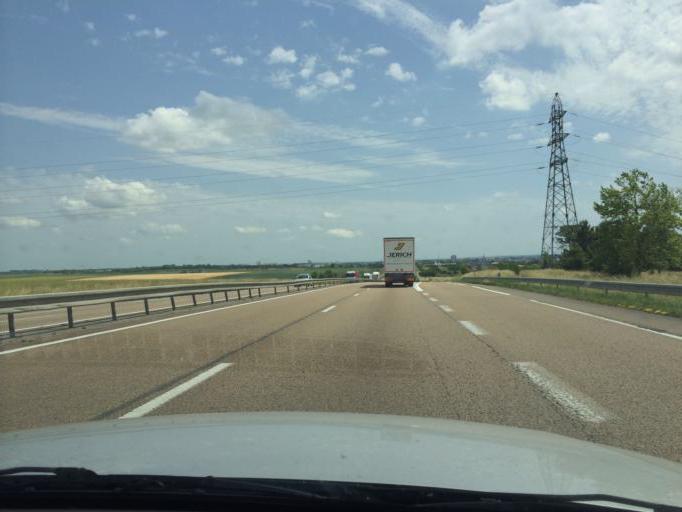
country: FR
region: Champagne-Ardenne
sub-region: Departement de la Marne
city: Fagnieres
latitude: 48.9956
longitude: 4.3416
